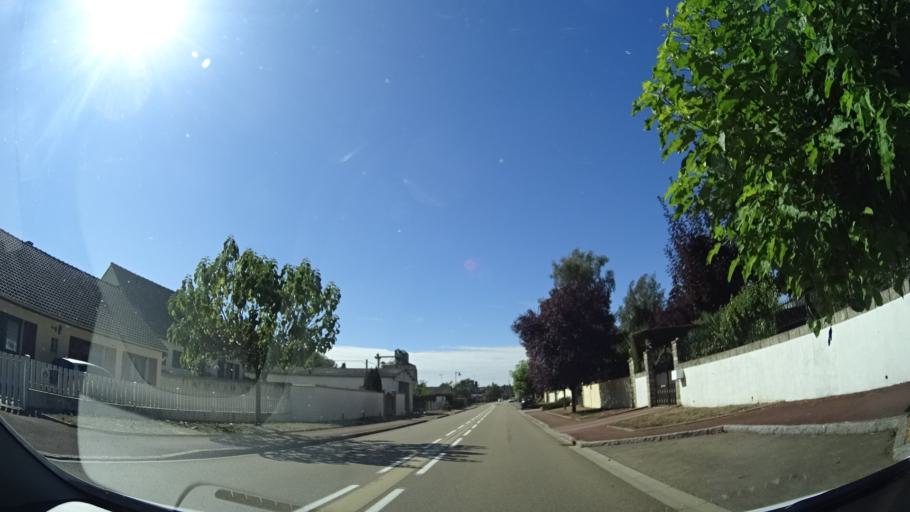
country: FR
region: Centre
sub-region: Departement du Loiret
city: Douchy
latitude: 47.9408
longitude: 3.0603
